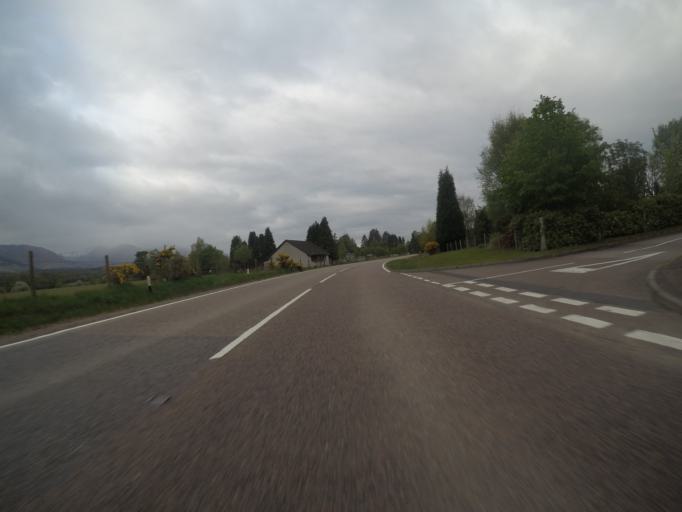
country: GB
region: Scotland
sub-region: Highland
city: Spean Bridge
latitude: 56.8895
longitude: -4.8578
